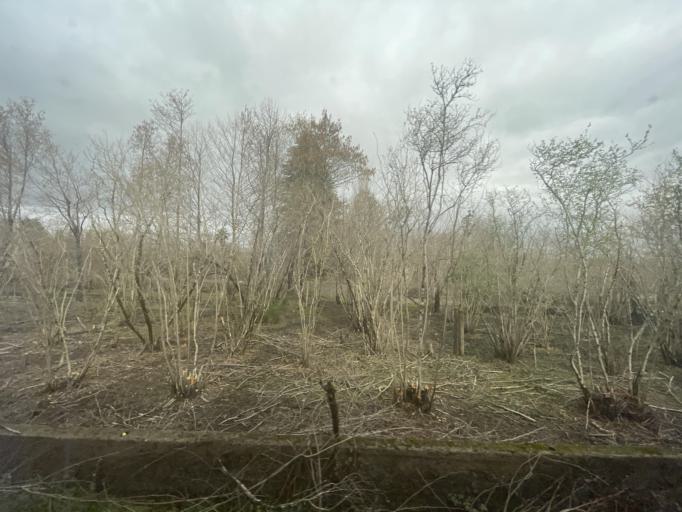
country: GE
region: Guria
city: Lanchkhuti
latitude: 42.0954
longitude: 42.0314
